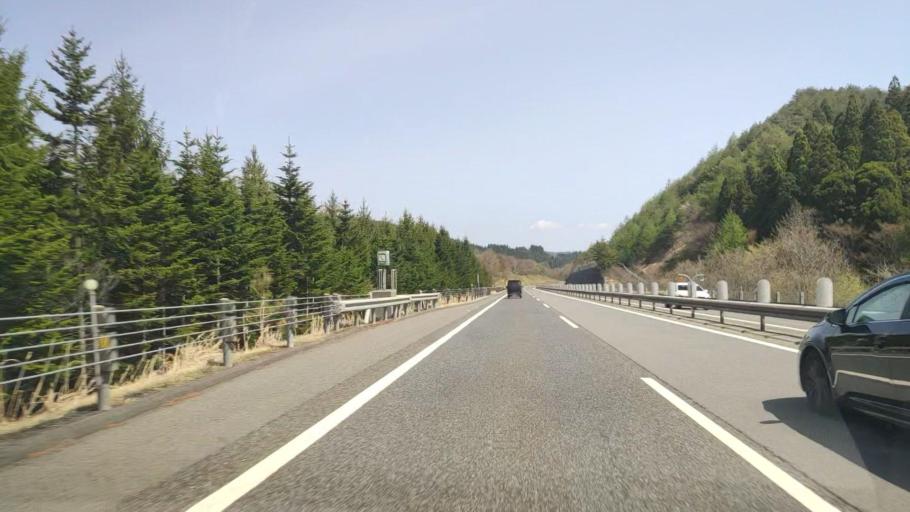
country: JP
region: Iwate
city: Ichinohe
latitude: 40.1307
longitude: 141.1029
